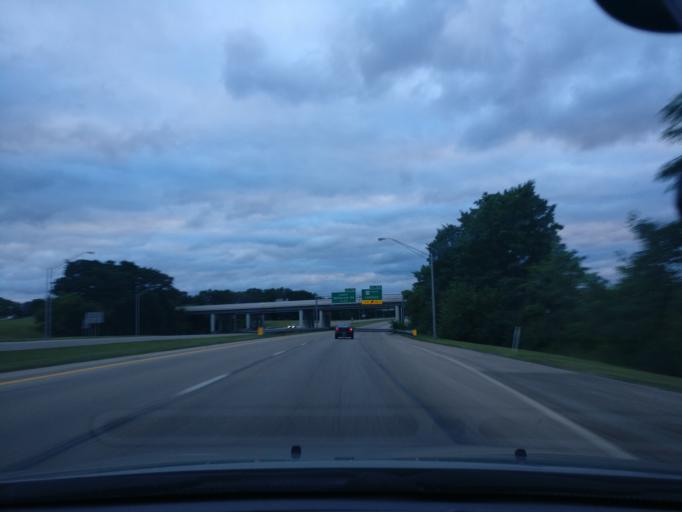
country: US
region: Ohio
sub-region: Greene County
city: Xenia
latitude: 39.6622
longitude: -83.9470
